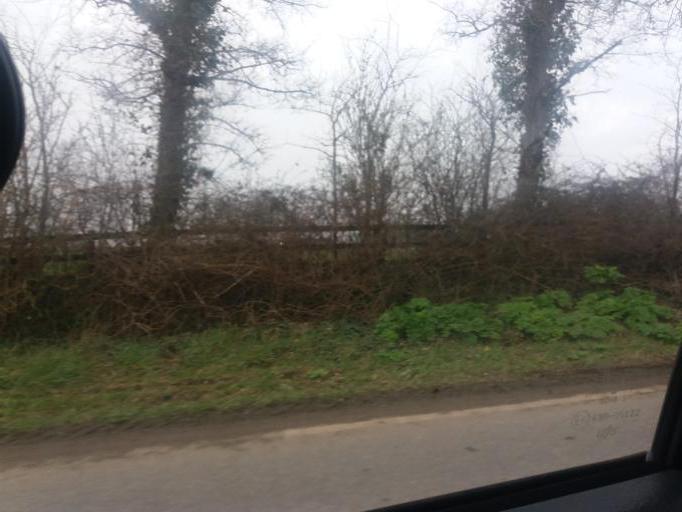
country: IE
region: Leinster
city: Portmarnock
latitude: 53.4236
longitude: -6.1598
